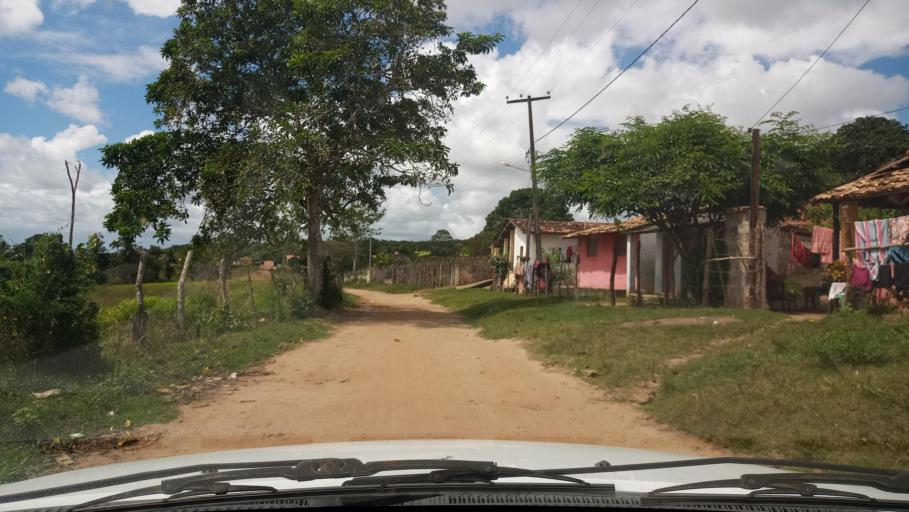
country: BR
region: Rio Grande do Norte
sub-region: Goianinha
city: Goianinha
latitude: -6.2616
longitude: -35.2594
